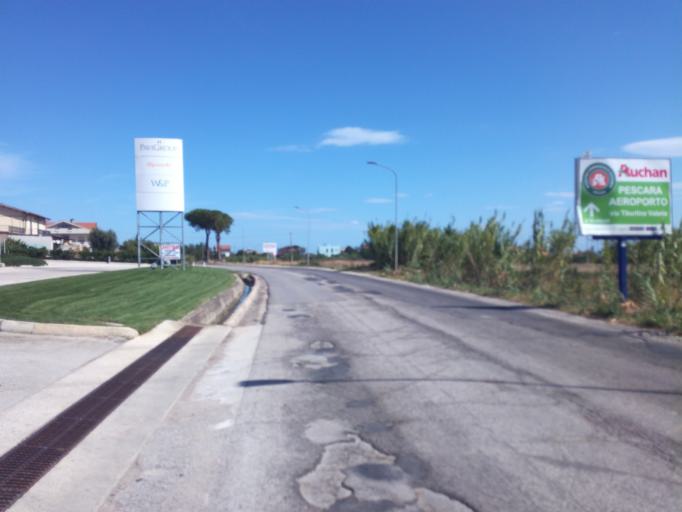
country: IT
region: Abruzzo
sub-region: Provincia di Chieti
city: Miglianico
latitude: 42.3874
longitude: 14.2956
